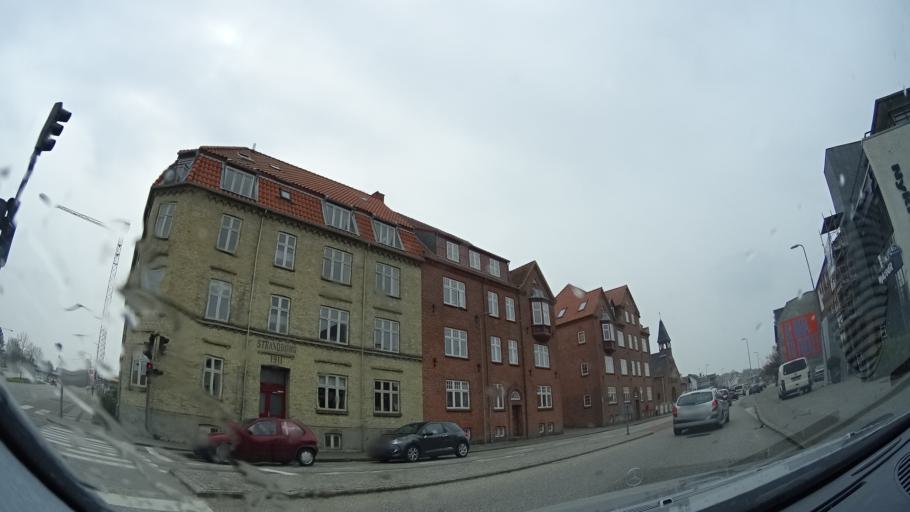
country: DK
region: Zealand
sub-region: Holbaek Kommune
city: Holbaek
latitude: 55.7191
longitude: 11.7061
